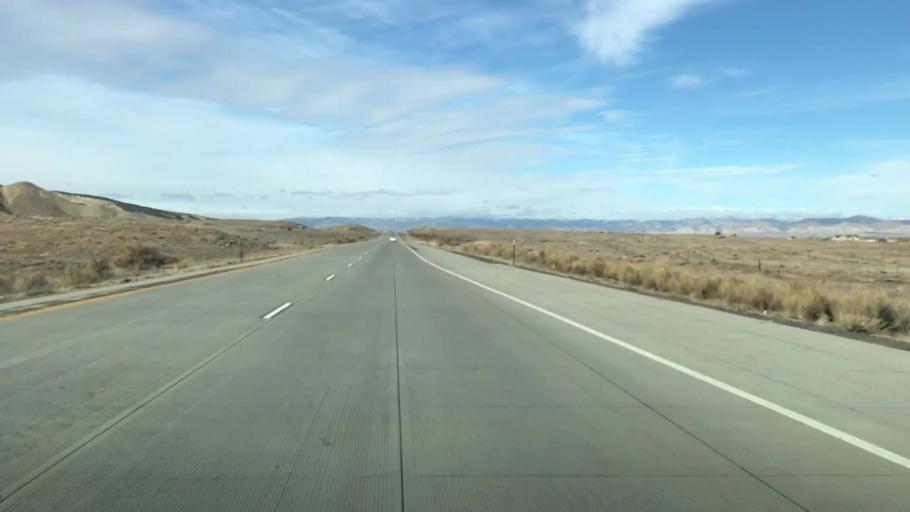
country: US
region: Colorado
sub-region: Mesa County
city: Loma
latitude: 39.1853
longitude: -108.8313
